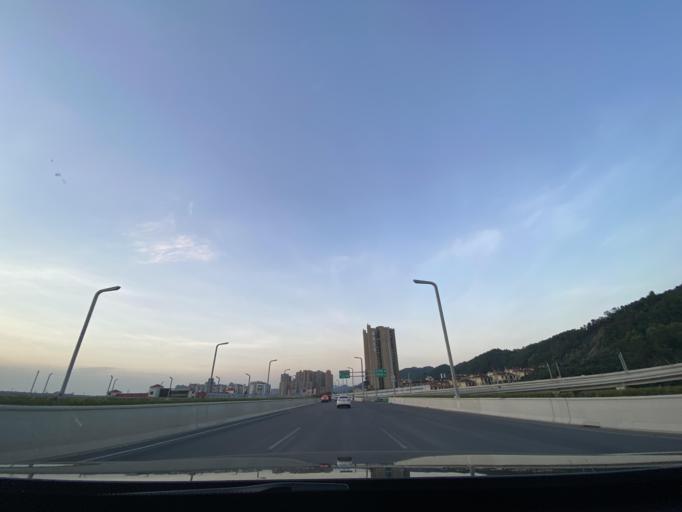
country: CN
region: Sichuan
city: Longquan
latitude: 30.5947
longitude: 104.3057
